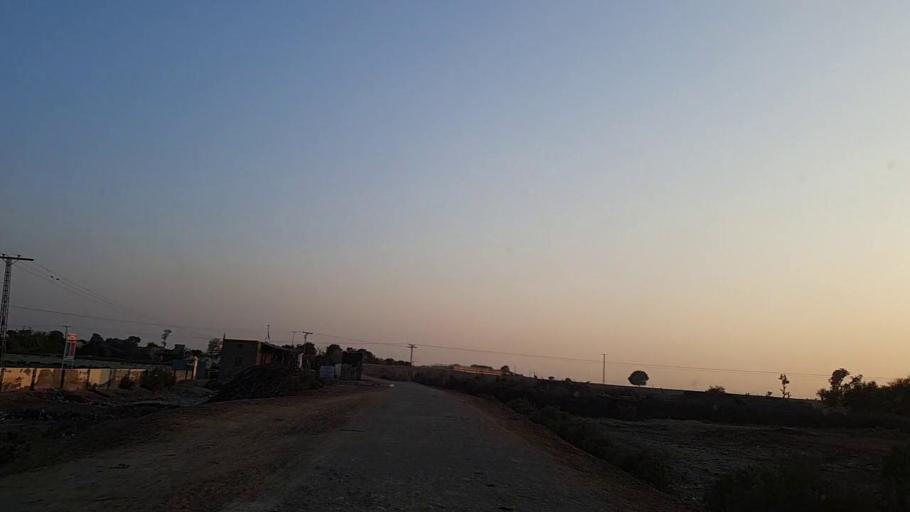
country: PK
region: Sindh
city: Bhit Shah
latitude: 25.9174
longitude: 68.5063
